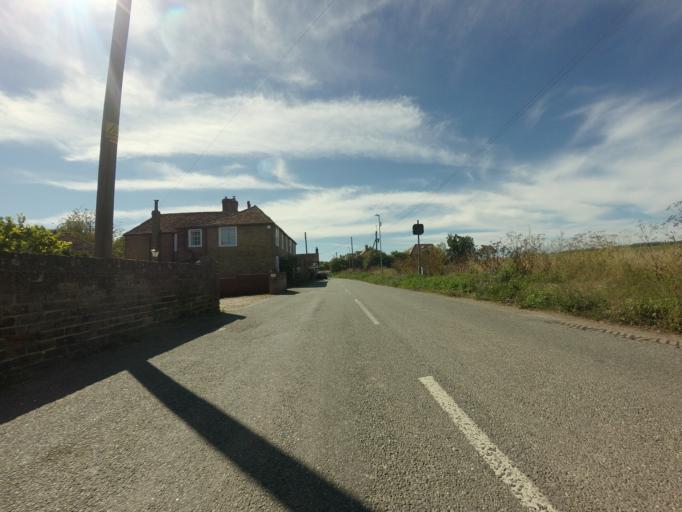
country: GB
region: England
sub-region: Kent
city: Birchington-on-Sea
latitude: 51.3375
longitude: 1.2875
